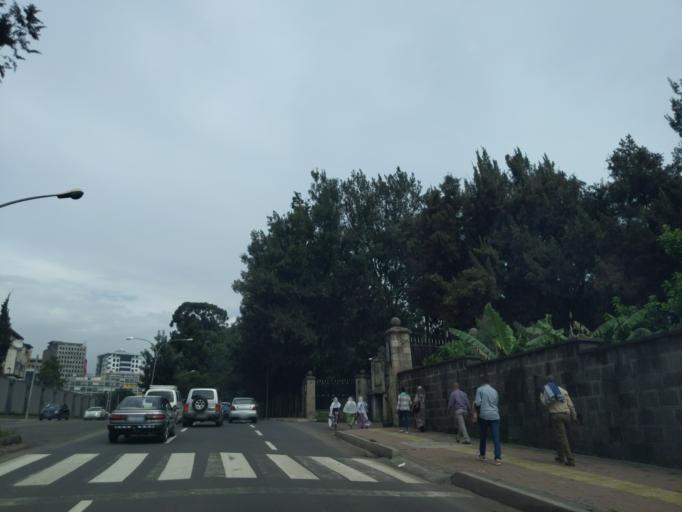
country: ET
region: Adis Abeba
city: Addis Ababa
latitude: 9.0180
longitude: 38.7610
